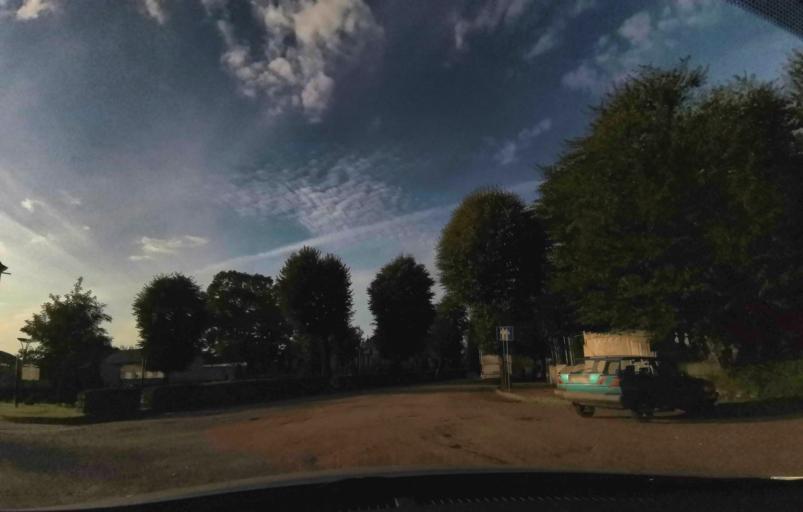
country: RU
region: Kaliningrad
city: Chernyakhovsk
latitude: 54.6290
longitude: 21.8195
